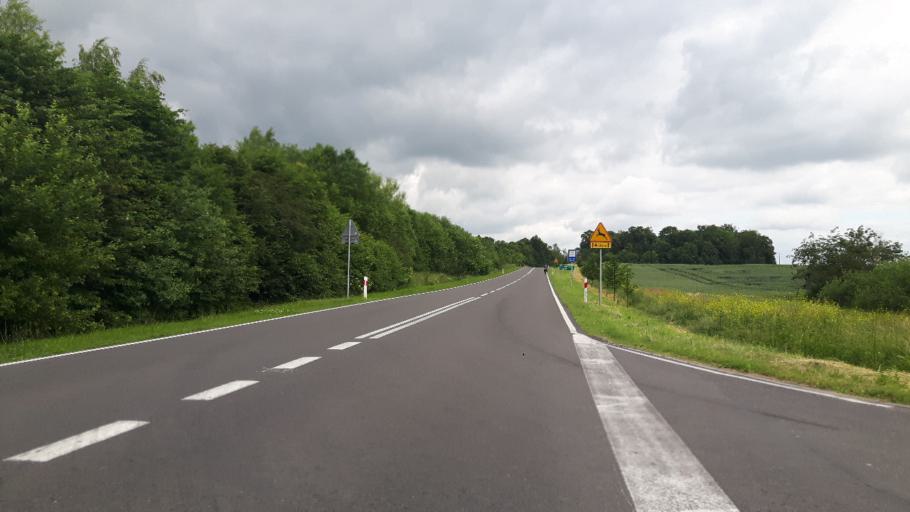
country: PL
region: West Pomeranian Voivodeship
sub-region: Powiat policki
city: Kolbaskowo
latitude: 53.3105
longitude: 14.4109
